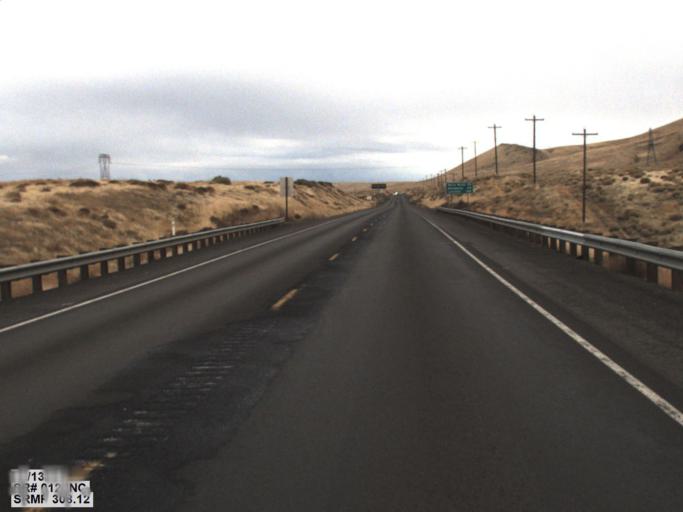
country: US
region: Washington
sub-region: Benton County
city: Finley
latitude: 46.0552
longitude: -118.8981
